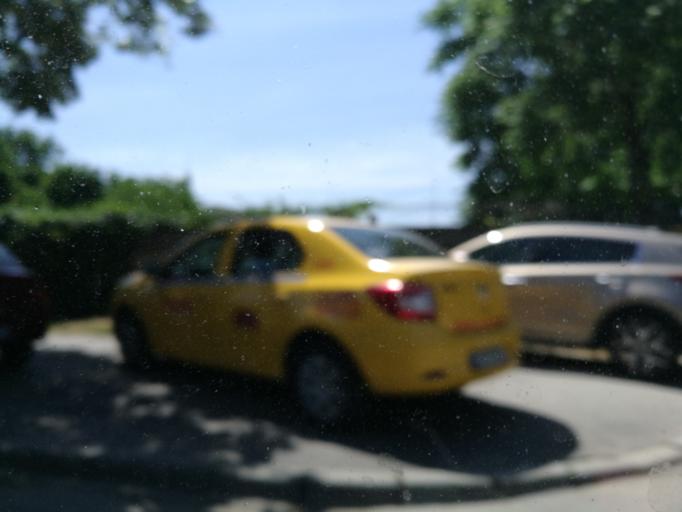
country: RO
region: Constanta
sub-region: Municipiul Constanta
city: Constanta
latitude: 44.2080
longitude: 28.6432
